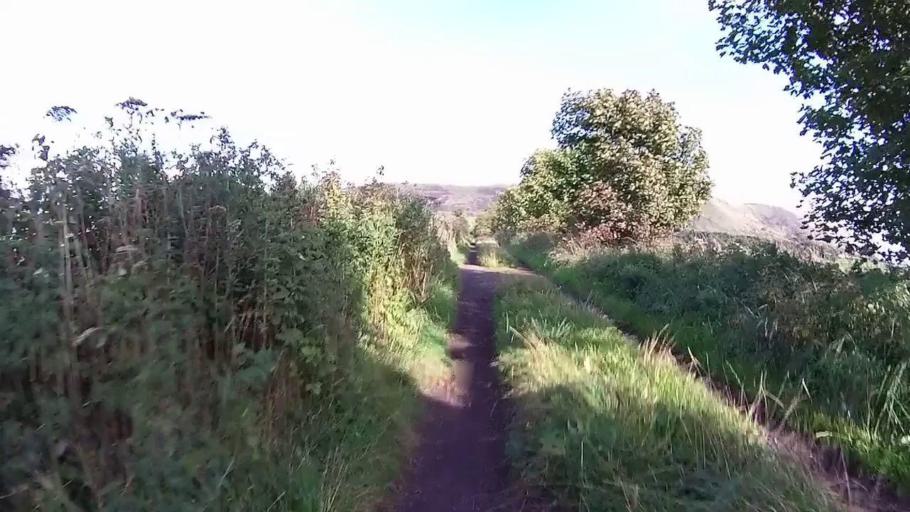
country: GB
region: Scotland
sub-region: Perth and Kinross
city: Milnathort
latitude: 56.2349
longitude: -3.3497
